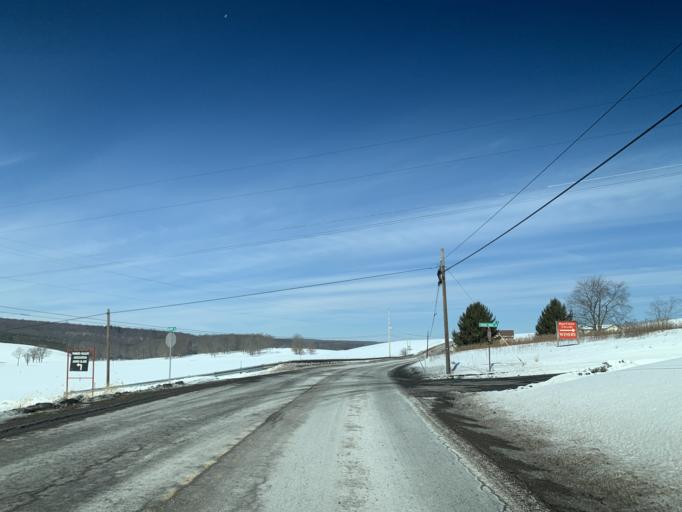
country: US
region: West Virginia
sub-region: Preston County
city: Terra Alta
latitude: 39.7108
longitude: -79.4453
